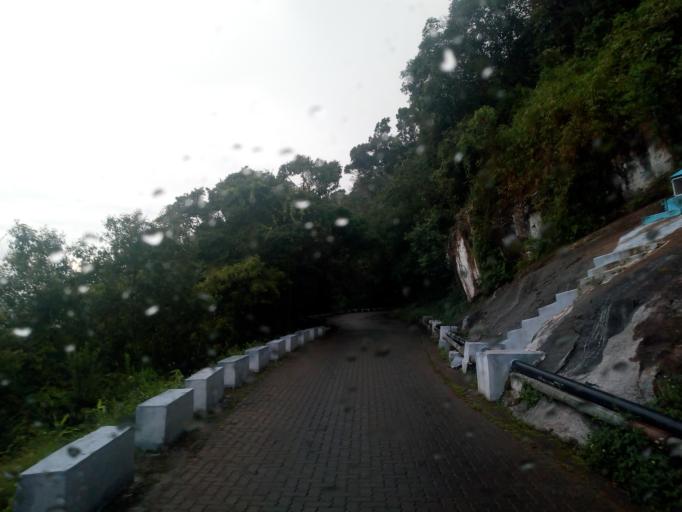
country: IN
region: Tamil Nadu
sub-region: Nilgiri
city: Wellington
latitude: 11.3507
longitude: 76.8280
